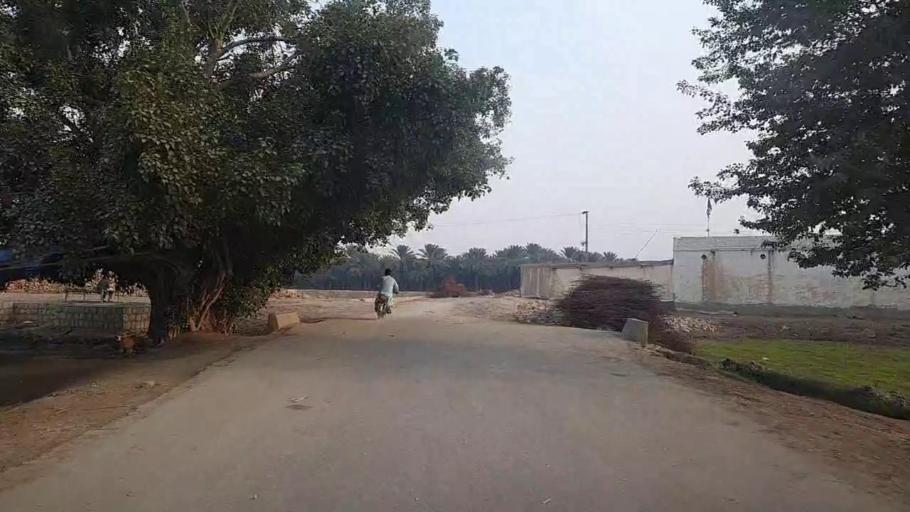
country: PK
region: Sindh
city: Kot Diji
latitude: 27.3836
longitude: 68.6616
